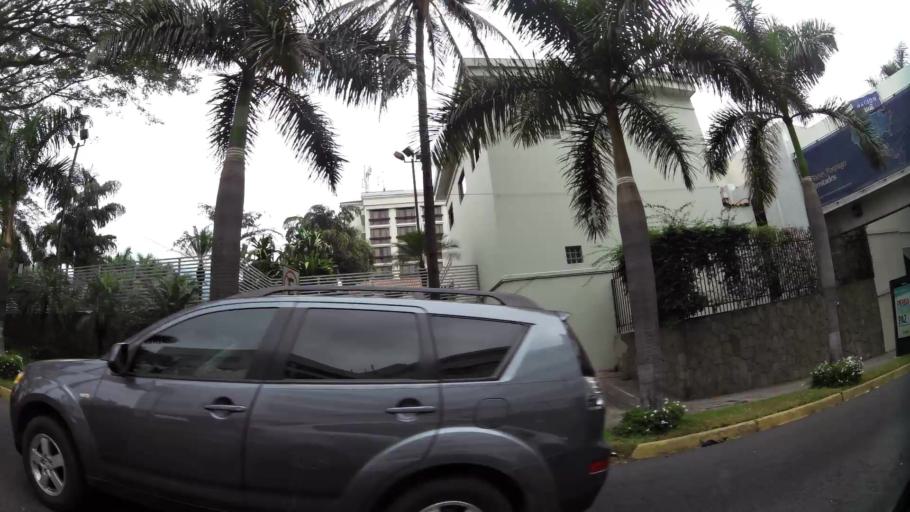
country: SV
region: San Salvador
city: Mejicanos
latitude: 13.7089
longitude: -89.2415
